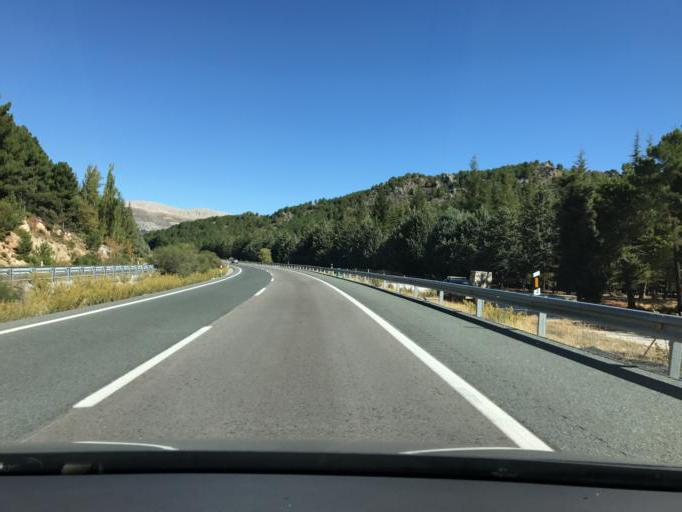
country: ES
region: Andalusia
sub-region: Provincia de Granada
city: Beas de Granada
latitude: 37.2748
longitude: -3.4595
